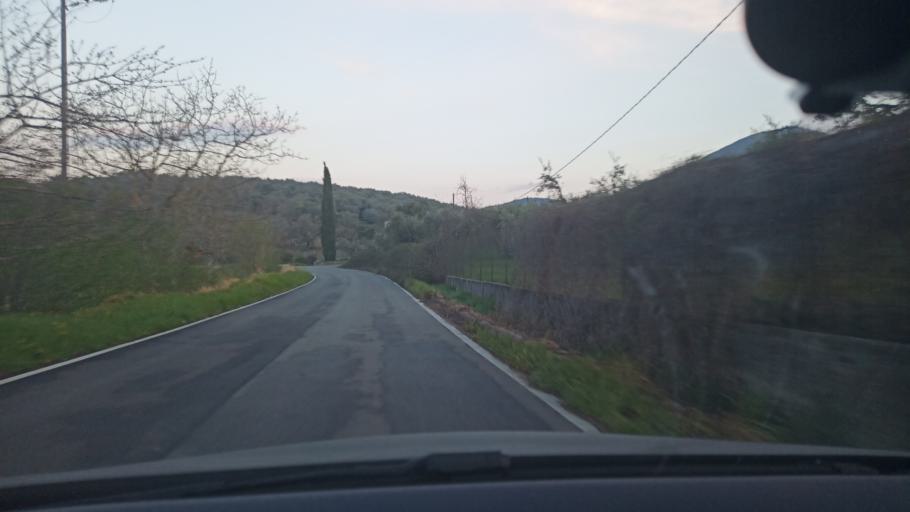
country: IT
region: Latium
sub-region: Provincia di Rieti
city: Vacone
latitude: 42.3652
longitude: 12.6599
